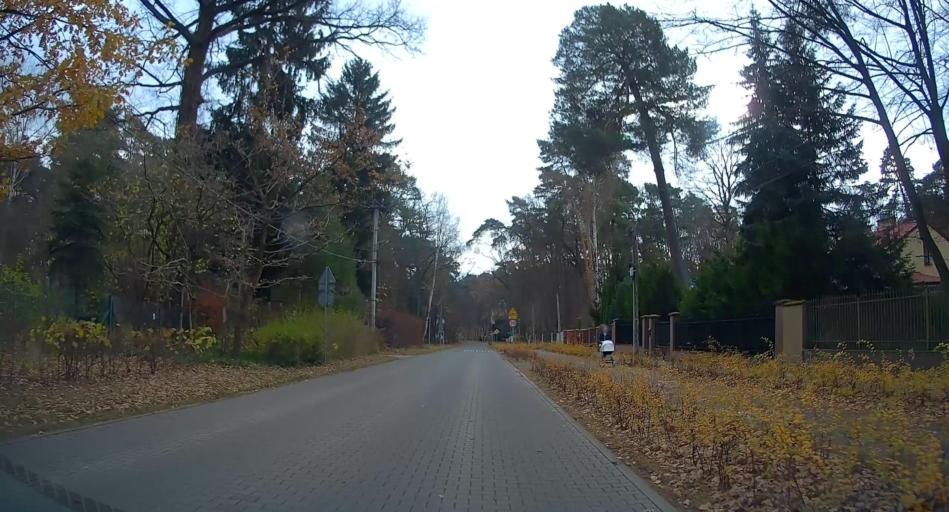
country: PL
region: Masovian Voivodeship
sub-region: Powiat piaseczynski
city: Piaseczno
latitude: 52.0562
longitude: 21.0185
